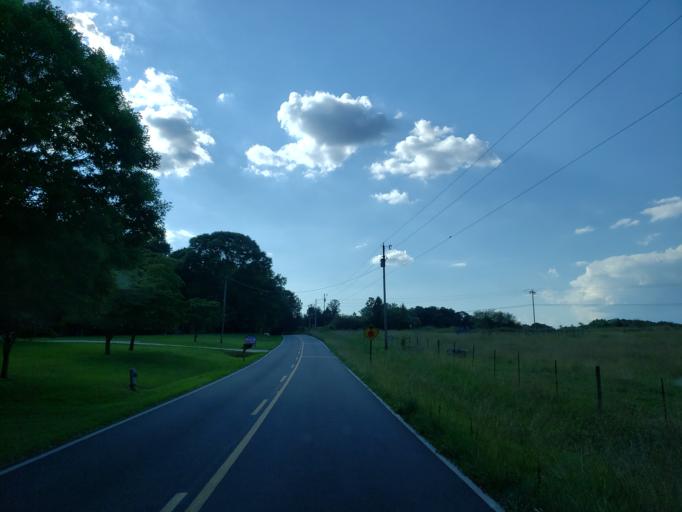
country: US
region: Georgia
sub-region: Haralson County
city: Bremen
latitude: 33.6711
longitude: -85.1182
